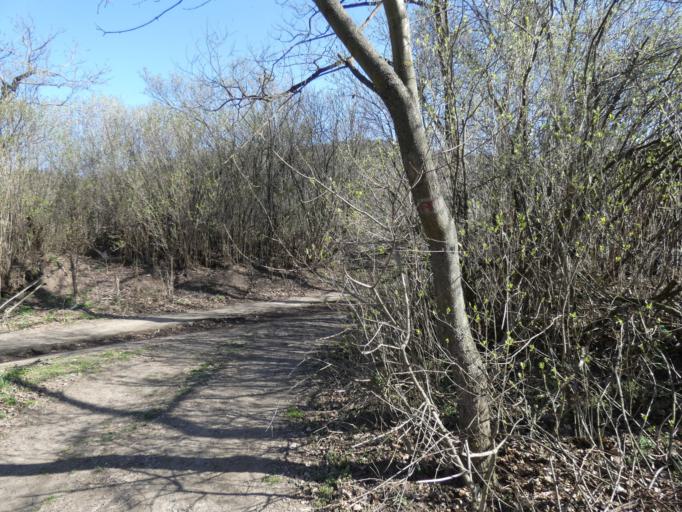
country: HU
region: Pest
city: Szob
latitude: 47.8666
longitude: 18.8819
